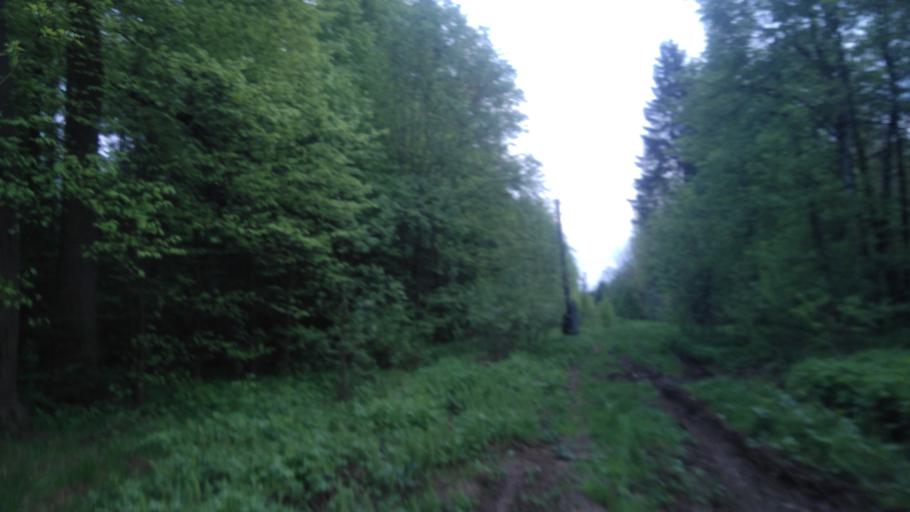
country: RU
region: Perm
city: Froly
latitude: 57.9659
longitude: 56.2911
